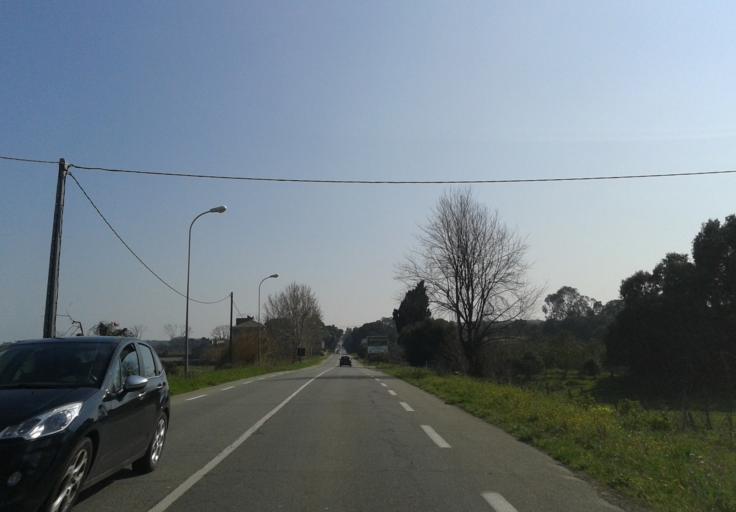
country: FR
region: Corsica
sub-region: Departement de la Haute-Corse
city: Cervione
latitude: 42.3120
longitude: 9.5420
